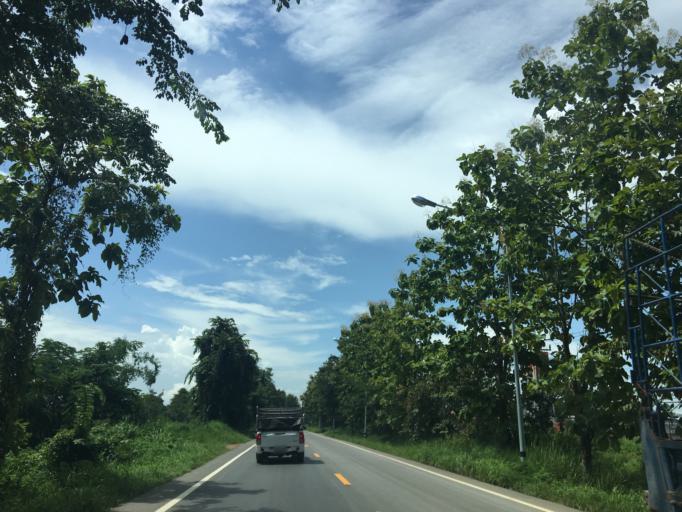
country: TH
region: Chiang Rai
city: Pa Daet
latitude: 19.5164
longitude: 99.9889
